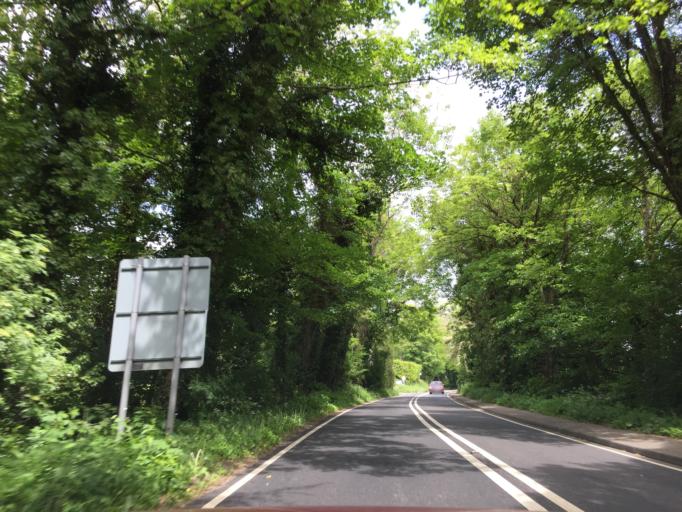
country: GB
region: England
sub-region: Gloucestershire
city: Stroud
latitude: 51.7700
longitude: -2.2179
